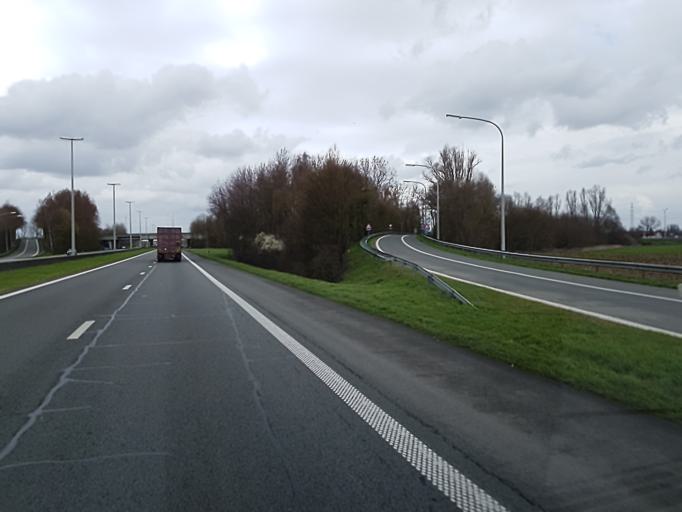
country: BE
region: Wallonia
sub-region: Province du Hainaut
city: Pecq
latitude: 50.6466
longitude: 3.2978
